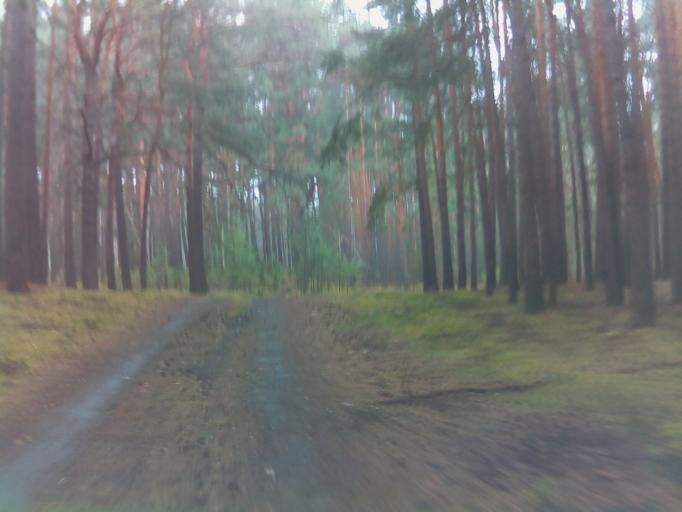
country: DE
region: Brandenburg
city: Jamlitz
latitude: 51.9846
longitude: 14.3667
